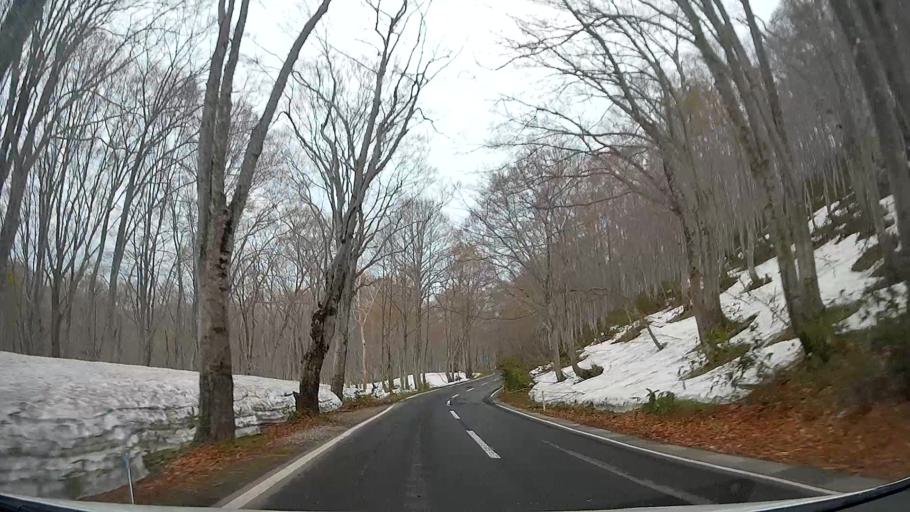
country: JP
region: Aomori
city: Aomori Shi
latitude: 40.6512
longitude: 140.8418
